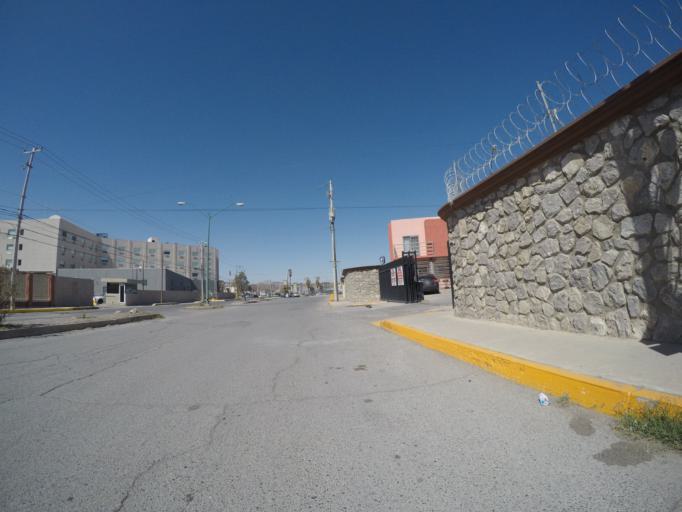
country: MX
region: Chihuahua
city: Ciudad Juarez
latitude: 31.6926
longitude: -106.4230
